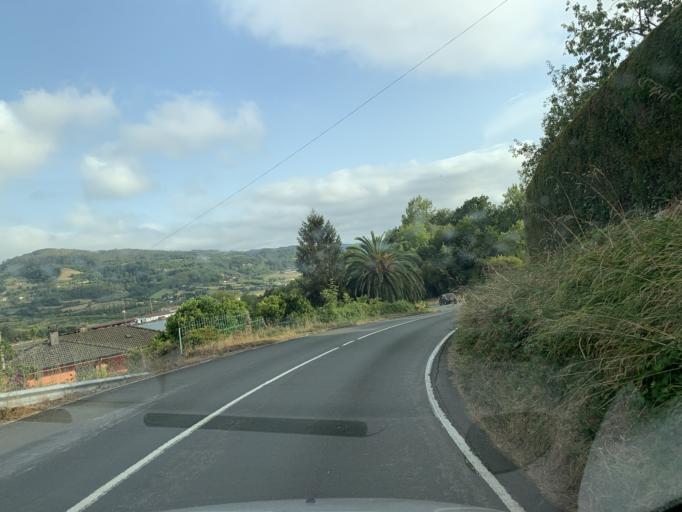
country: ES
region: Asturias
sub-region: Province of Asturias
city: Villaviciosa
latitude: 43.5032
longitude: -5.4280
